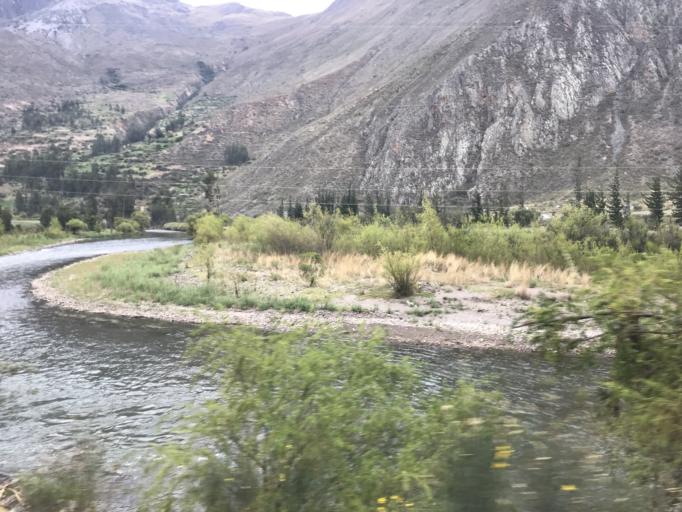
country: PE
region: Cusco
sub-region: Provincia de Urubamba
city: Ollantaytambo
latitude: -13.2420
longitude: -72.2944
